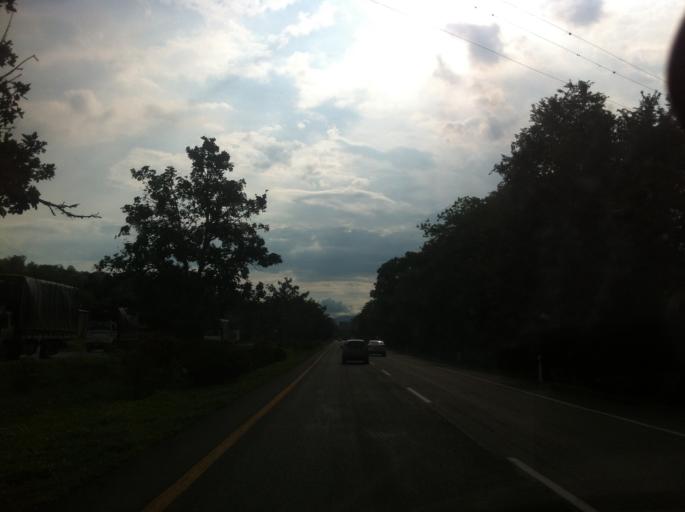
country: CO
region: Valle del Cauca
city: San Pedro
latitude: 3.9764
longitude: -76.2469
